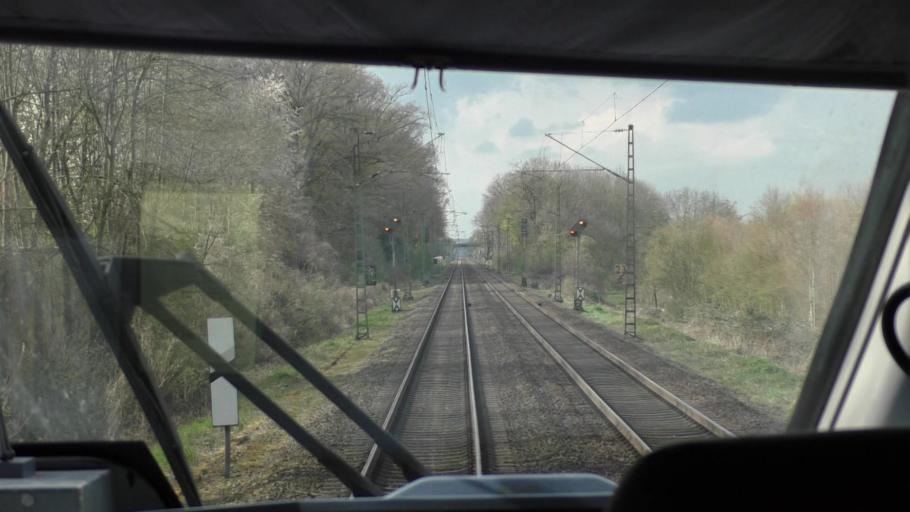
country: DE
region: North Rhine-Westphalia
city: Bornheim
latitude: 50.7672
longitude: 6.9983
